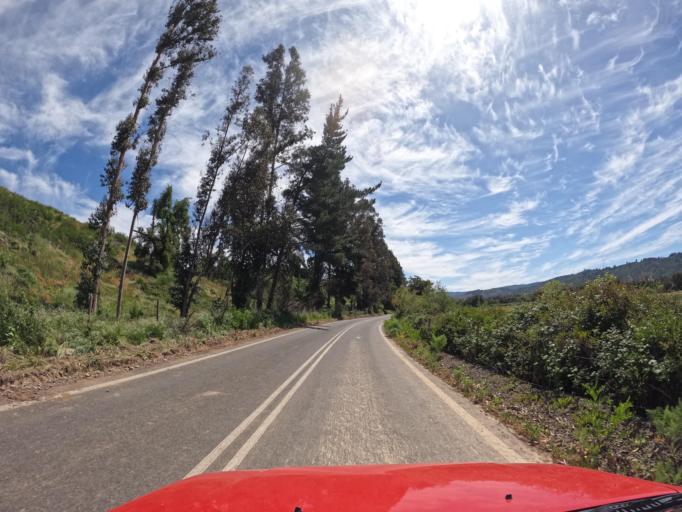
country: CL
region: Maule
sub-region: Provincia de Talca
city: Talca
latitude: -34.9933
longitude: -71.8614
